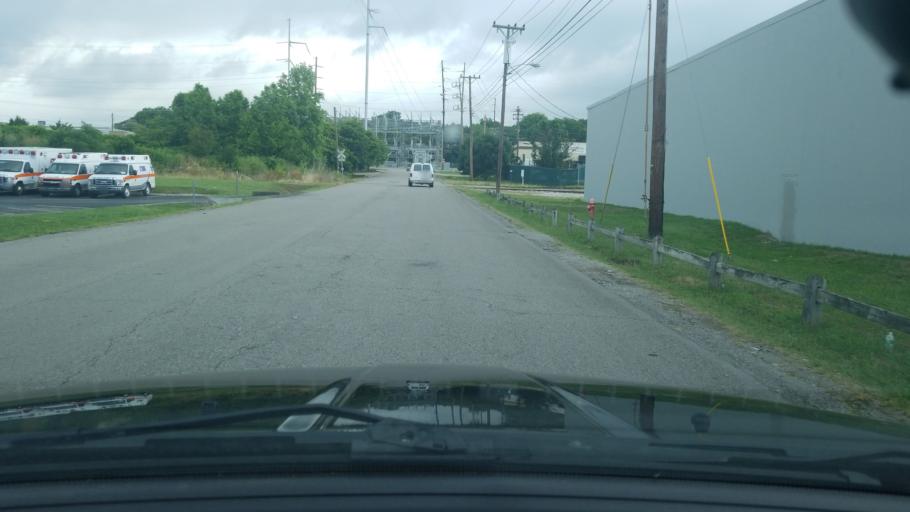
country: US
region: Tennessee
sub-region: Davidson County
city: Oak Hill
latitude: 36.0948
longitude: -86.7465
